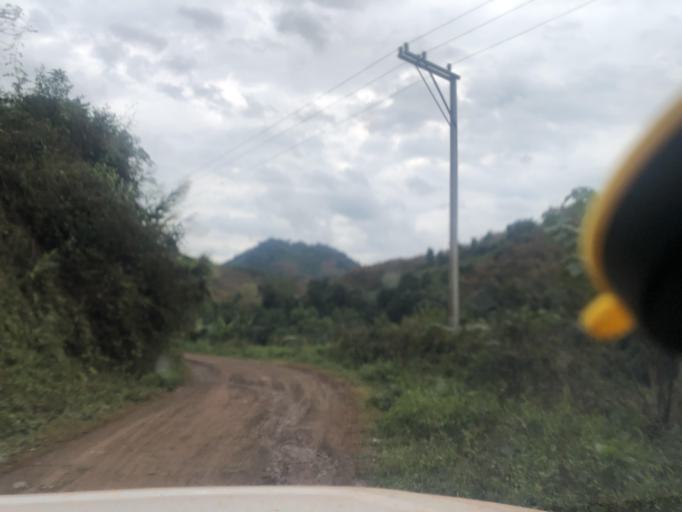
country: LA
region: Phongsali
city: Phongsali
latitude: 21.4333
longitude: 102.0305
